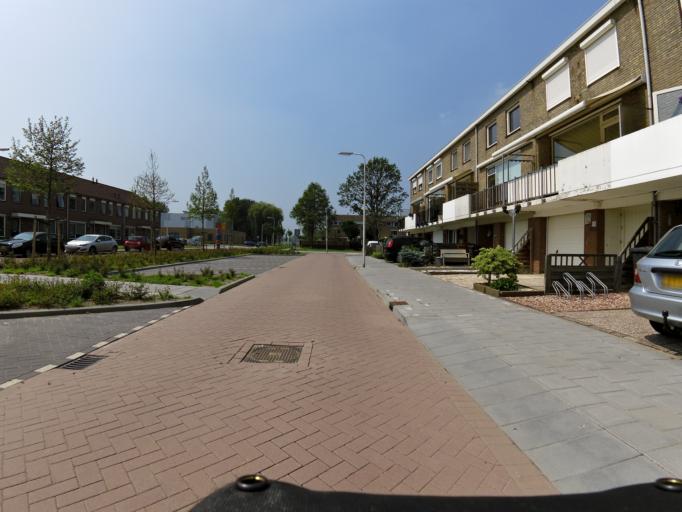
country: NL
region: South Holland
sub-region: Gemeente Maassluis
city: Maassluis
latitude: 51.8662
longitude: 4.2421
